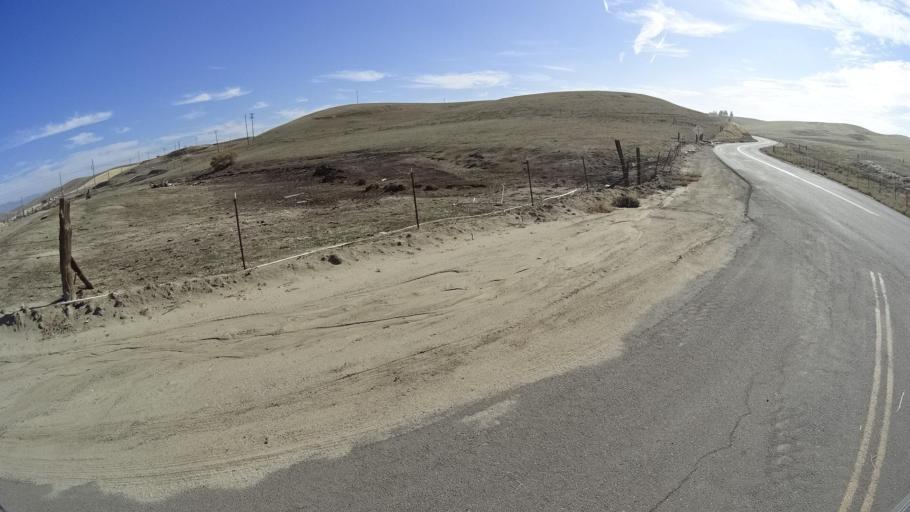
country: US
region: California
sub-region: Kern County
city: Oildale
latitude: 35.6256
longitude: -118.9876
